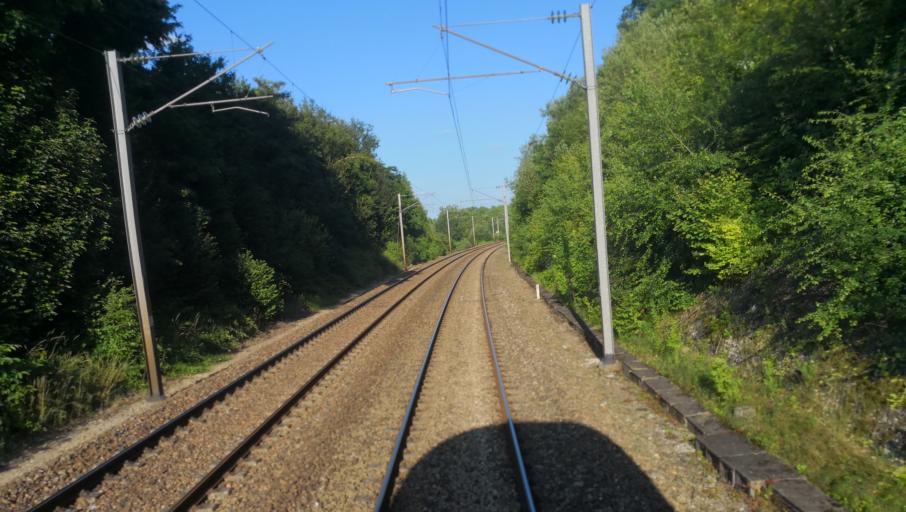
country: FR
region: Haute-Normandie
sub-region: Departement de l'Eure
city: Breuilpont
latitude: 48.9653
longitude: 1.4039
